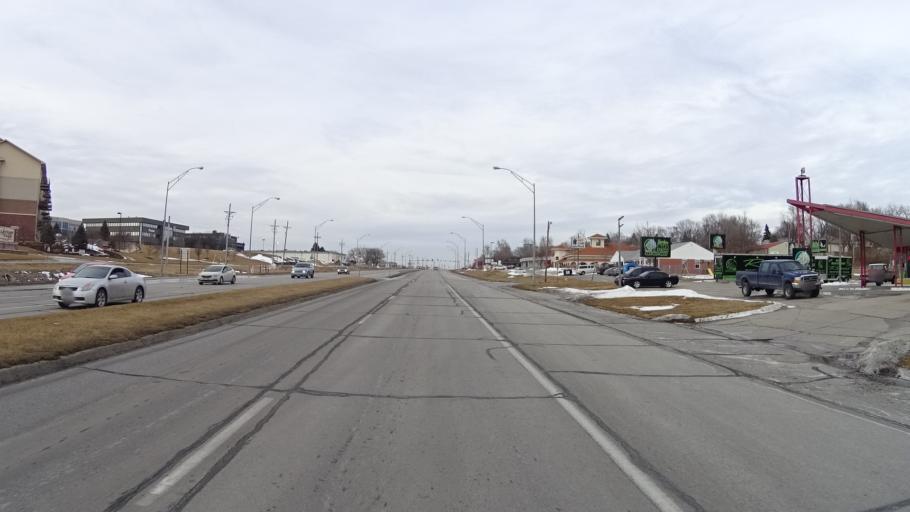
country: US
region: Nebraska
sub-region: Sarpy County
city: Offutt Air Force Base
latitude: 41.1436
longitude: -95.9268
